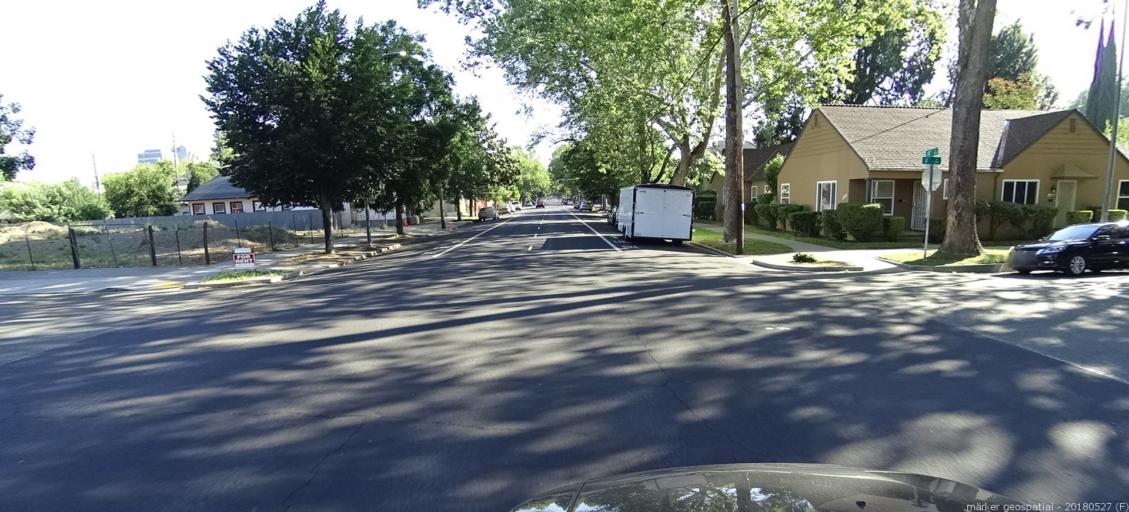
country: US
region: California
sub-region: Sacramento County
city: Sacramento
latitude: 38.5681
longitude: -121.4988
